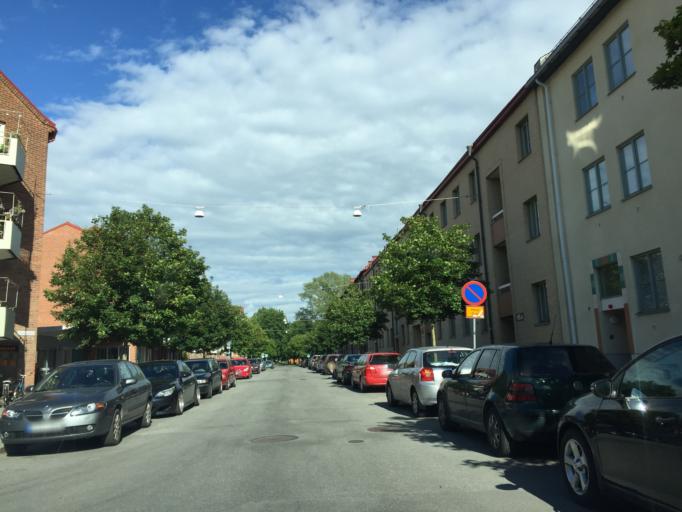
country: SE
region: OErebro
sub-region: Orebro Kommun
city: Orebro
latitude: 59.2818
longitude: 15.2252
